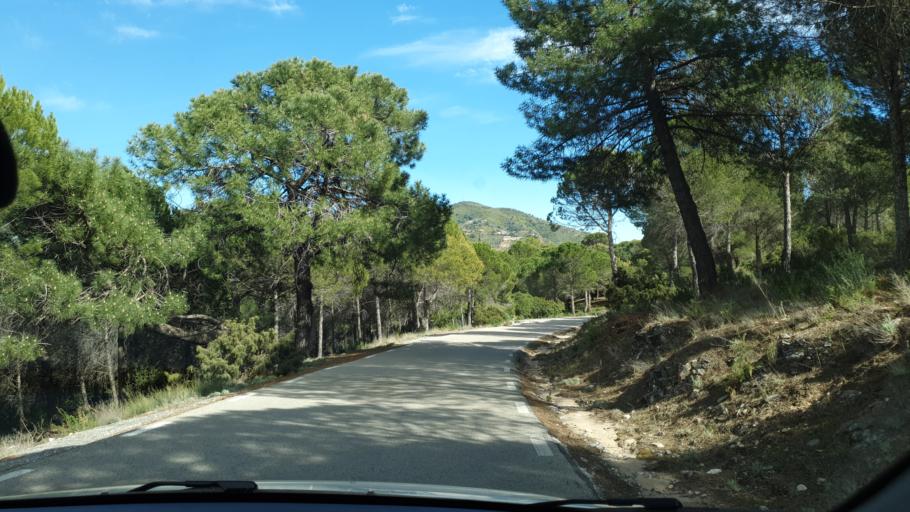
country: ES
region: Andalusia
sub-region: Provincia de Malaga
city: Ojen
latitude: 36.5878
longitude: -4.8629
